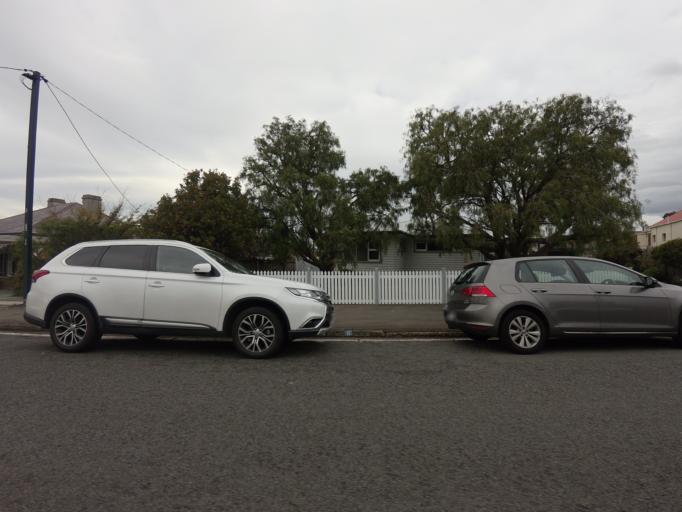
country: AU
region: Tasmania
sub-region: Clarence
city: Bellerive
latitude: -42.8757
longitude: 147.3659
